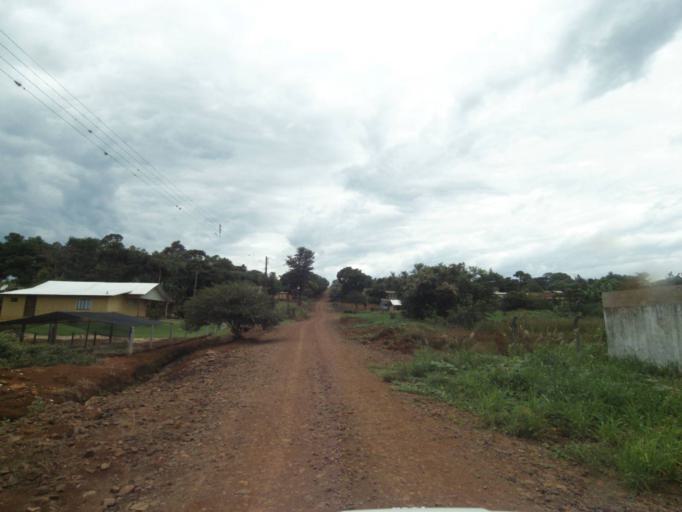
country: BR
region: Parana
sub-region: Guaraniacu
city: Guaraniacu
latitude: -24.9194
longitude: -52.9362
